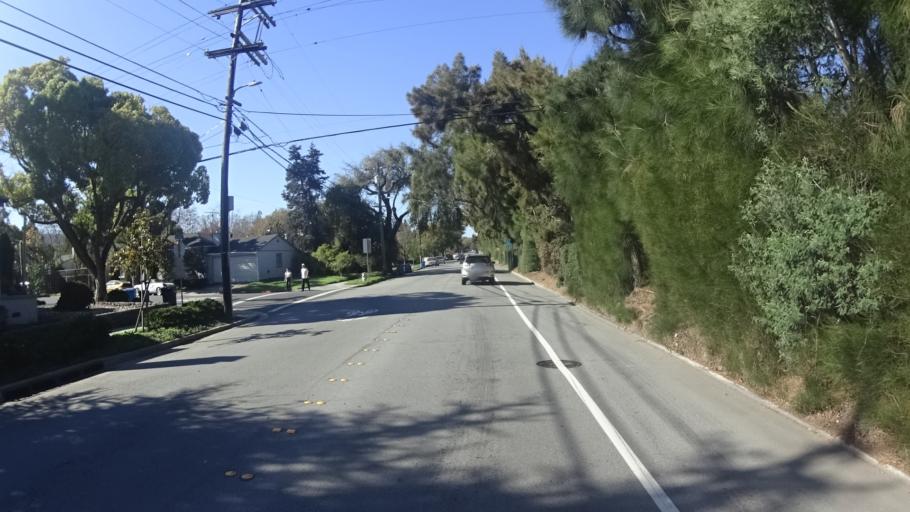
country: US
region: California
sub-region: San Mateo County
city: Burlingame
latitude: 37.5896
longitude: -122.3683
